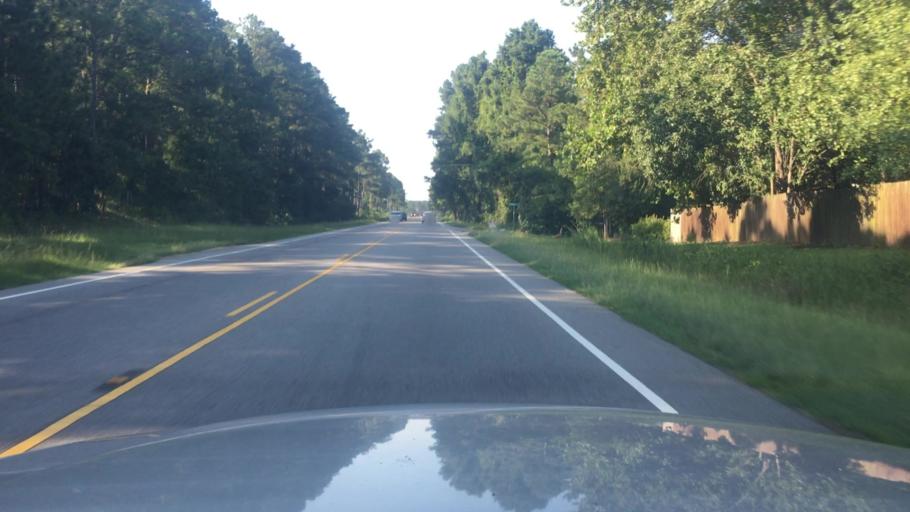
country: US
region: North Carolina
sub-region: Harnett County
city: Walkertown
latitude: 35.2007
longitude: -78.8494
